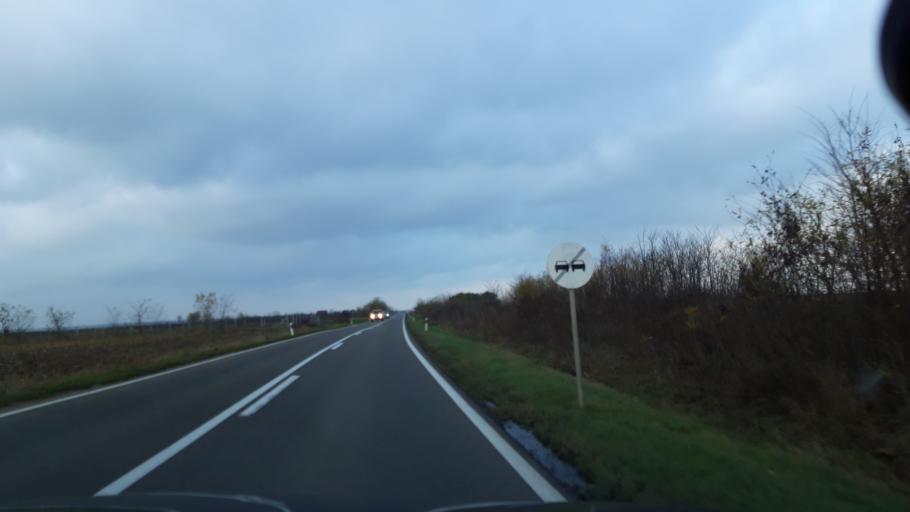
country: RS
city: Sanad
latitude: 45.9897
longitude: 20.1089
